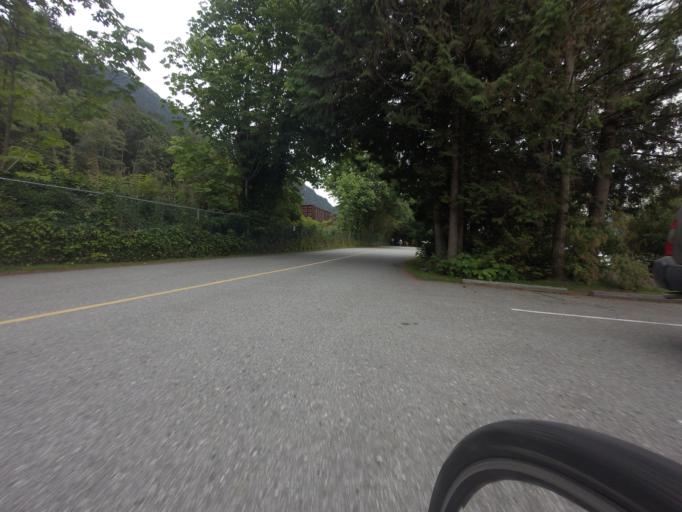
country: CA
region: British Columbia
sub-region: Greater Vancouver Regional District
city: Lions Bay
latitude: 49.5585
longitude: -123.2349
